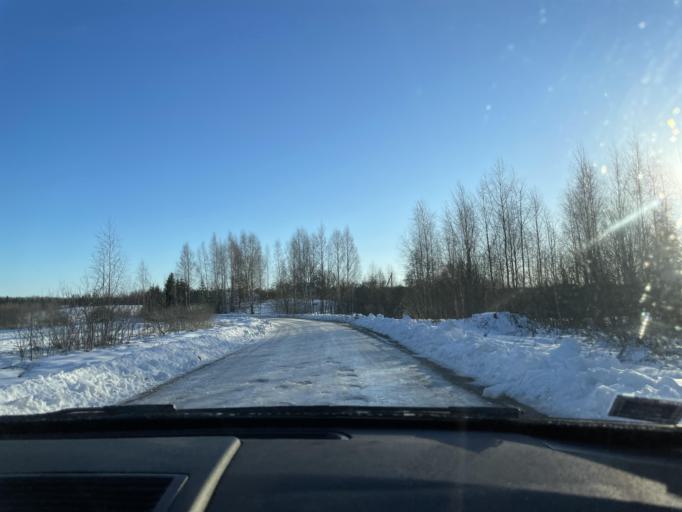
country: LV
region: Ludzas Rajons
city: Ludza
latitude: 56.4614
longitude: 27.6085
